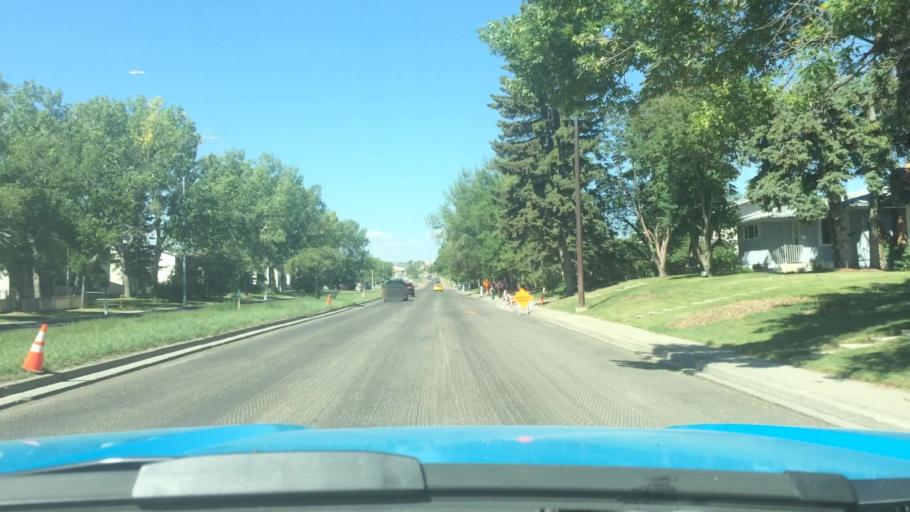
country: CA
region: Alberta
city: Calgary
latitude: 51.0530
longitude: -113.9660
